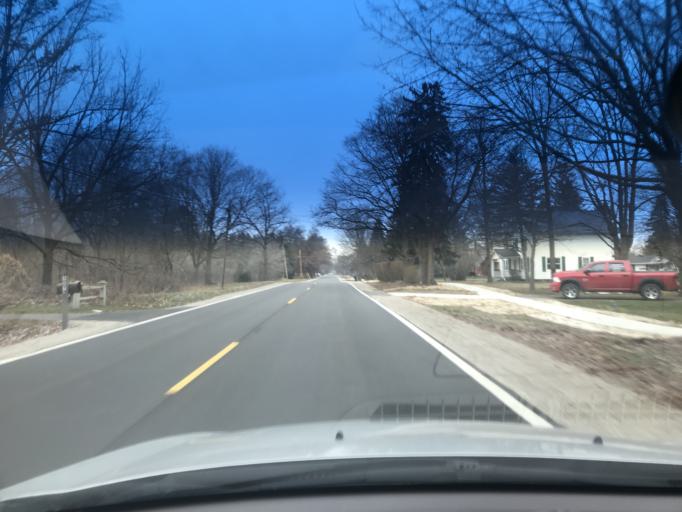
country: US
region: Michigan
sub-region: Macomb County
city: Shelby
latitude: 42.6625
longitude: -83.0580
